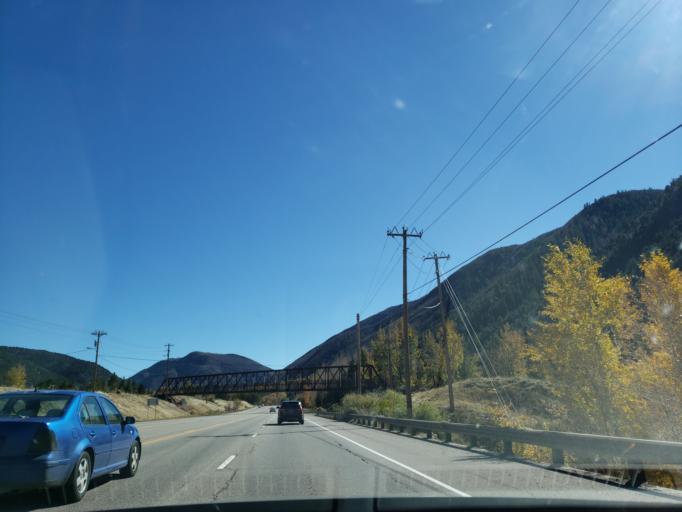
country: US
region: Colorado
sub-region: Eagle County
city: Basalt
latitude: 39.3479
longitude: -107.0132
